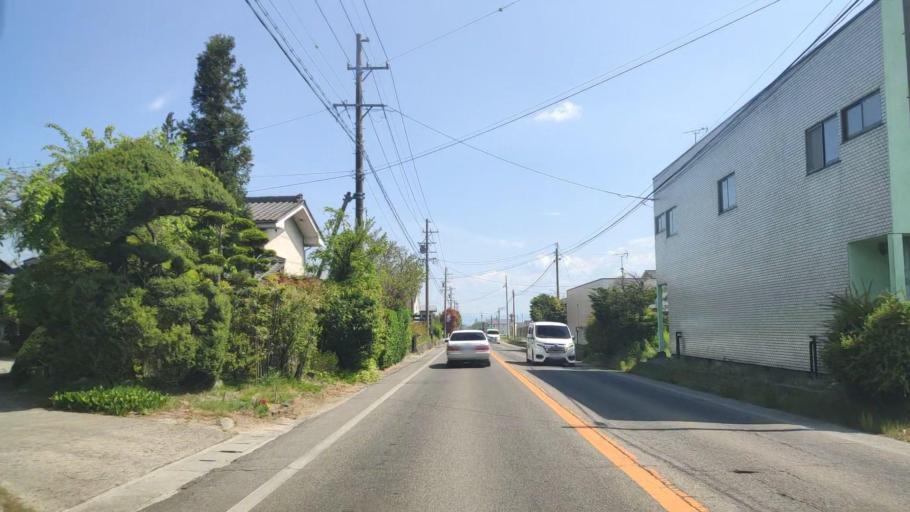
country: JP
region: Nagano
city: Hotaka
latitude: 36.3933
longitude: 137.8636
